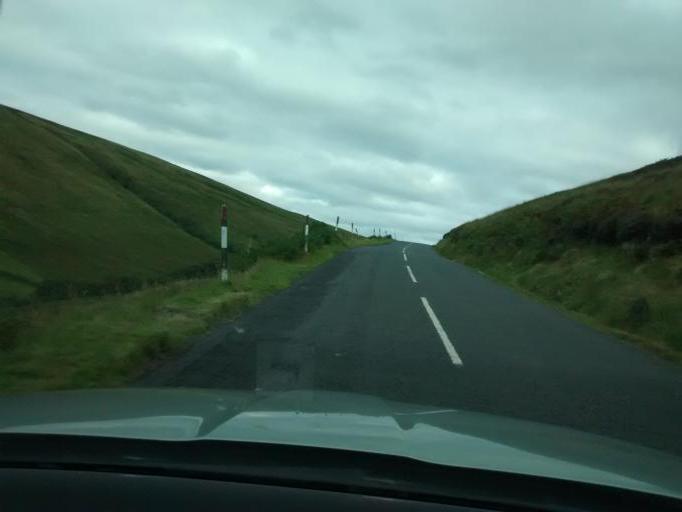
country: GB
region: Scotland
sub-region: North Ayrshire
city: Isle of Arran
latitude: 55.6922
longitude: -5.2440
